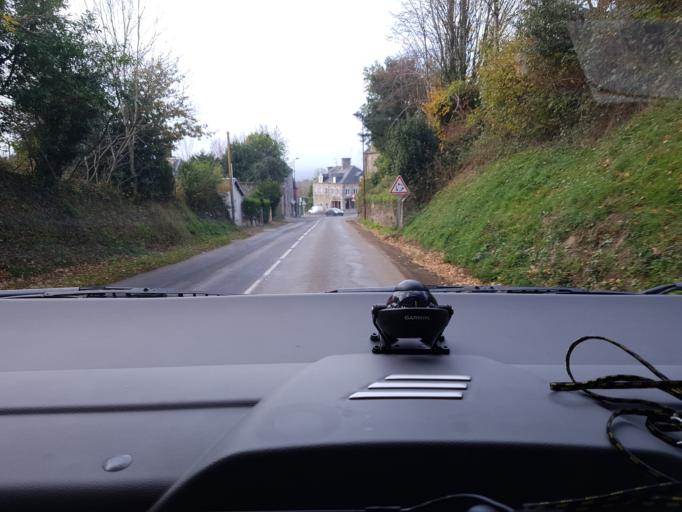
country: FR
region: Lower Normandy
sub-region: Departement du Calvados
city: Saint-Sever-Calvados
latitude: 48.7507
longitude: -1.0651
